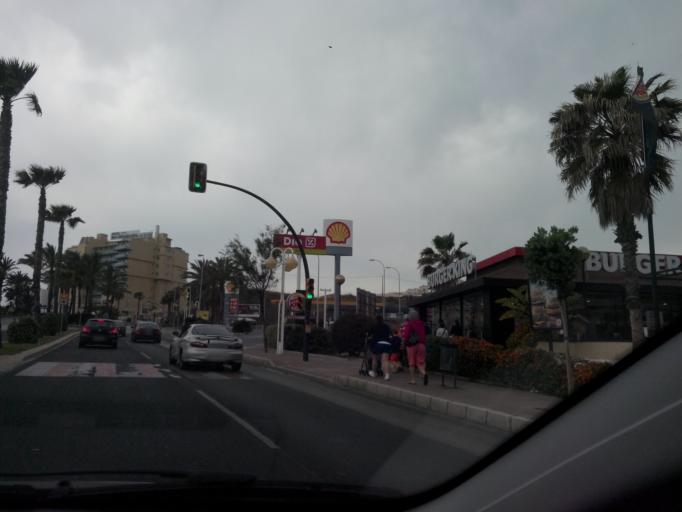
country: ES
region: Andalusia
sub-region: Provincia de Malaga
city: Benalmadena
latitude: 36.5838
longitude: -4.5349
